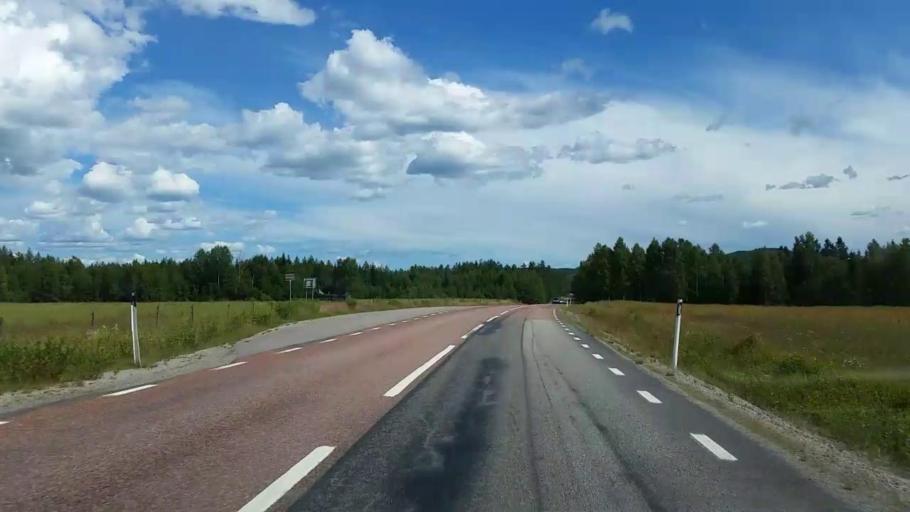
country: SE
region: Gaevleborg
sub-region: Ovanakers Kommun
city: Edsbyn
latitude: 61.3466
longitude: 15.6402
